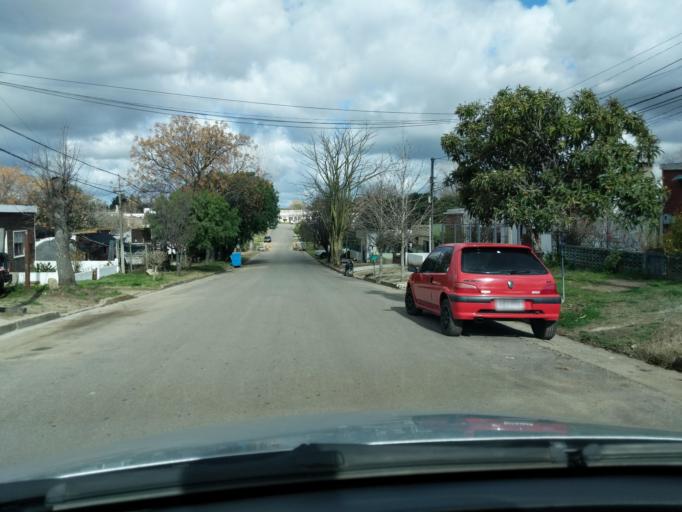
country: UY
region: Florida
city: Florida
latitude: -34.0914
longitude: -56.2290
